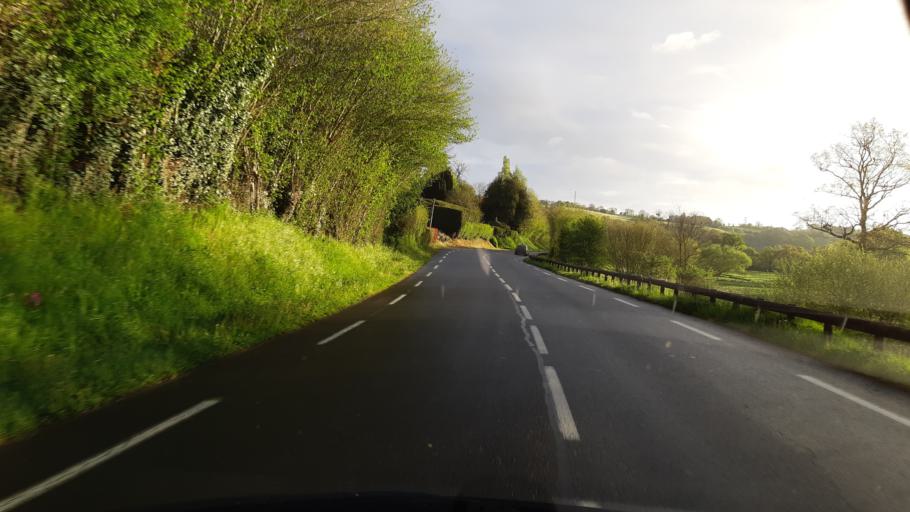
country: FR
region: Lower Normandy
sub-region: Departement de la Manche
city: Agneaux
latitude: 49.0839
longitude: -1.1162
